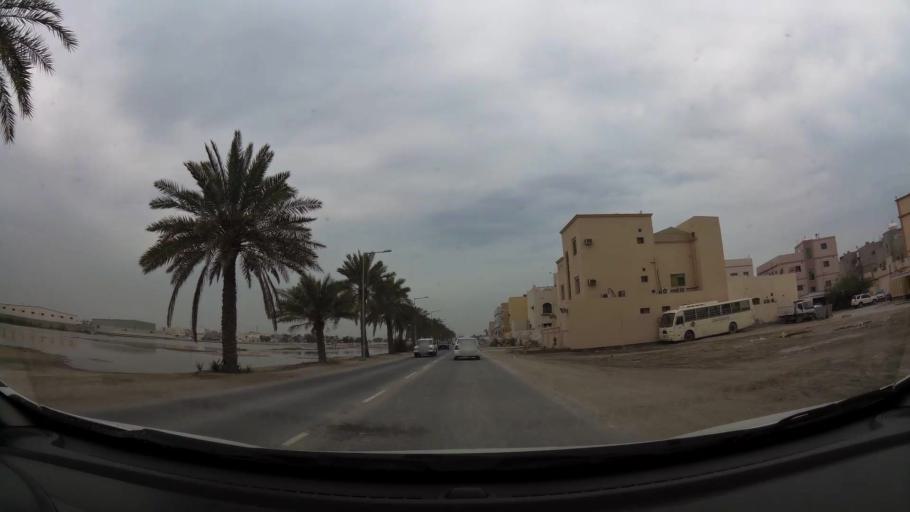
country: BH
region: Northern
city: Sitrah
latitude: 26.1682
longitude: 50.6215
